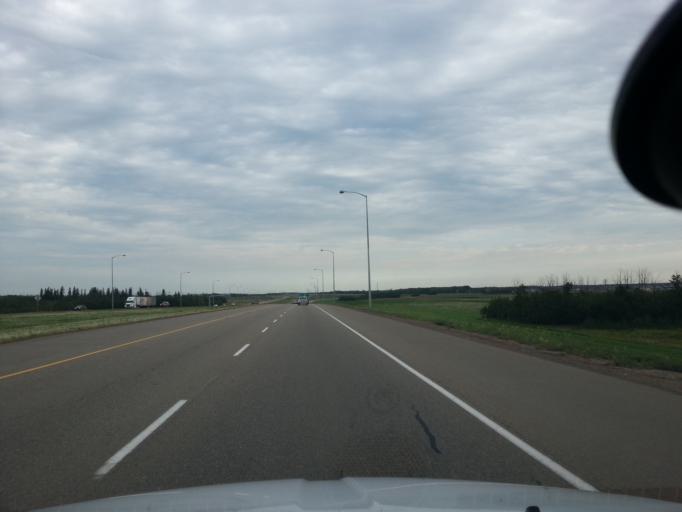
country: CA
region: Alberta
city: St. Albert
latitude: 53.6331
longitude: -113.5634
